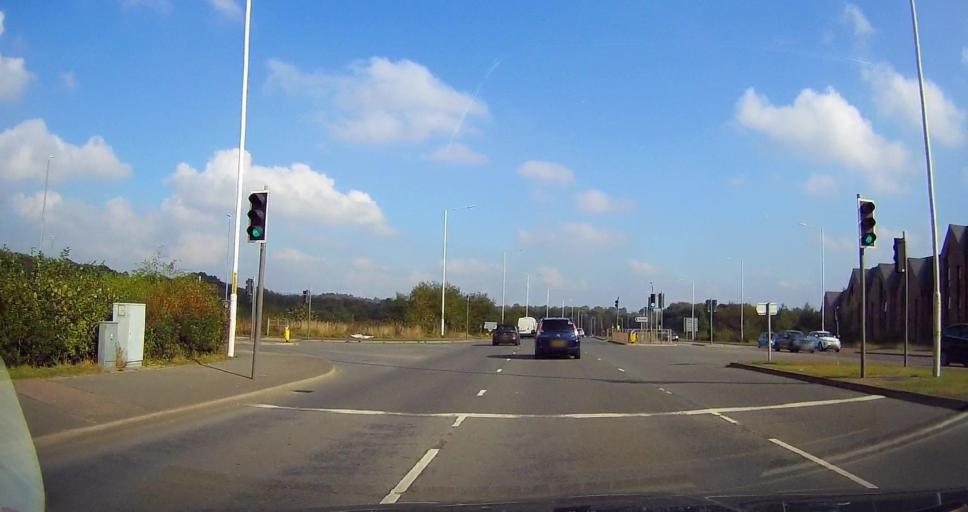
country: GB
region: England
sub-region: Kent
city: Ashford
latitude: 51.1580
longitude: 0.8615
